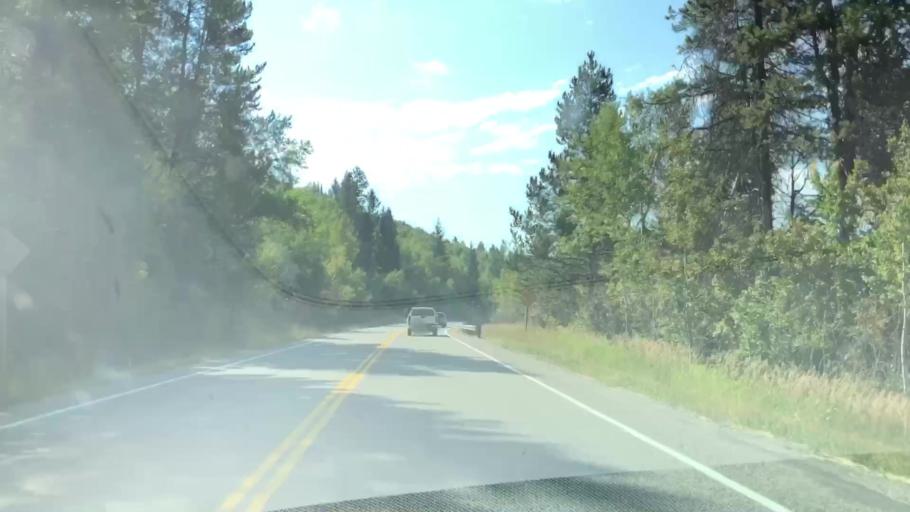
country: US
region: Idaho
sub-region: Teton County
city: Victor
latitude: 43.3233
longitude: -111.1667
